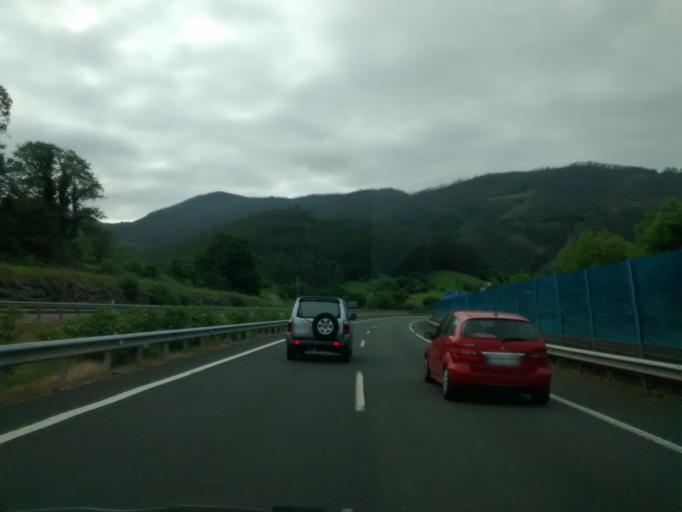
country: ES
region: Cantabria
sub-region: Provincia de Cantabria
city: Los Corrales de Buelna
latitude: 43.2765
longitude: -4.0793
